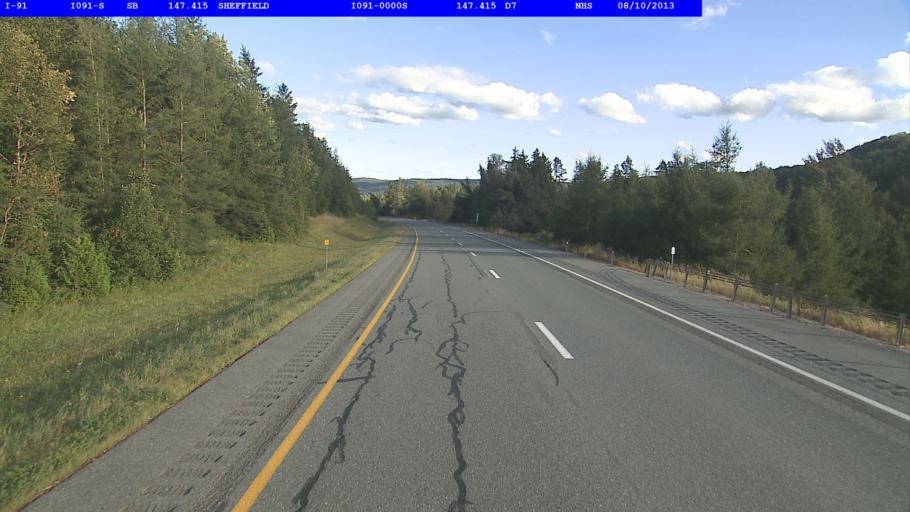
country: US
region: Vermont
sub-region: Caledonia County
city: Lyndonville
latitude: 44.6275
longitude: -72.1291
